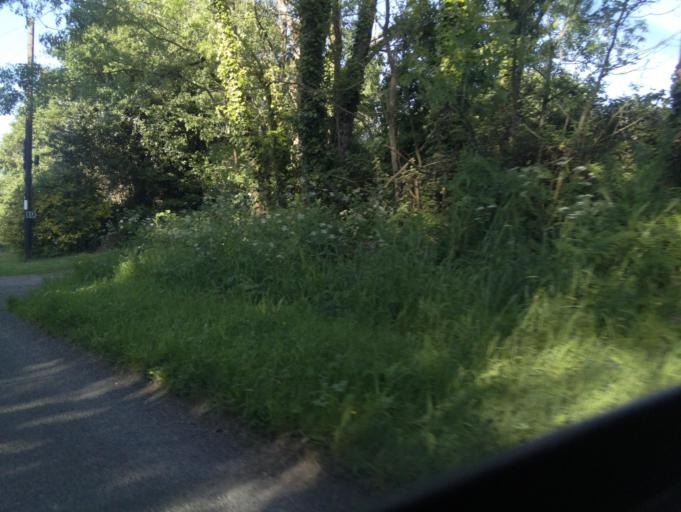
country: GB
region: England
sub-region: Dorset
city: Lyme Regis
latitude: 50.7959
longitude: -2.8686
